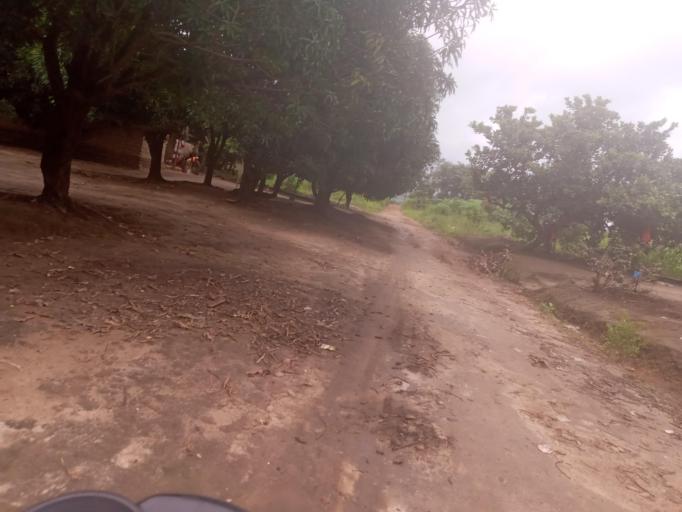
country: SL
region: Northern Province
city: Bumbuna
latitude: 8.9514
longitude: -11.7582
